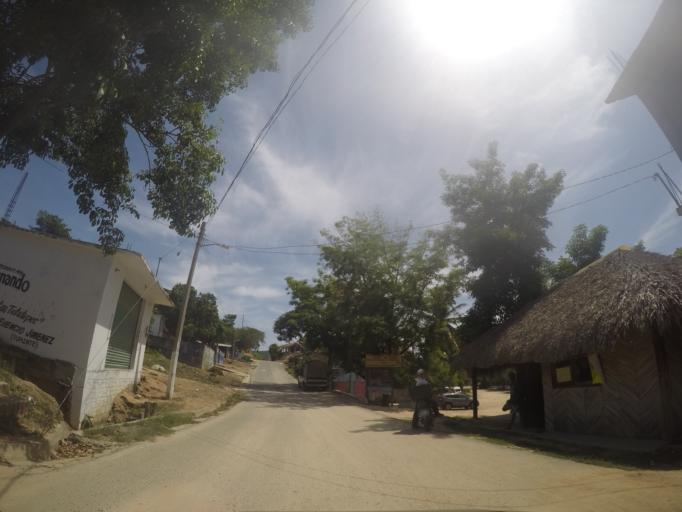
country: MX
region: Oaxaca
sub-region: Villa de Tututepec de Melchor Ocampo
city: Santa Rosa de Lima
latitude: 15.9875
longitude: -97.5499
